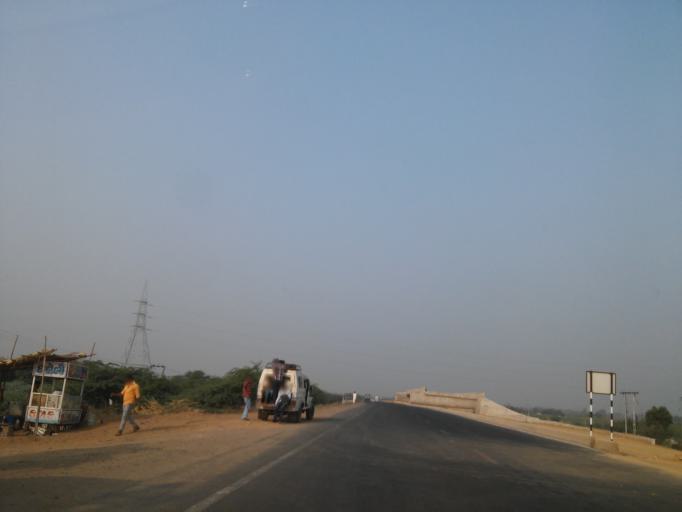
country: IN
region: Gujarat
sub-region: Kachchh
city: Anjar
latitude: 23.2942
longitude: 70.0768
